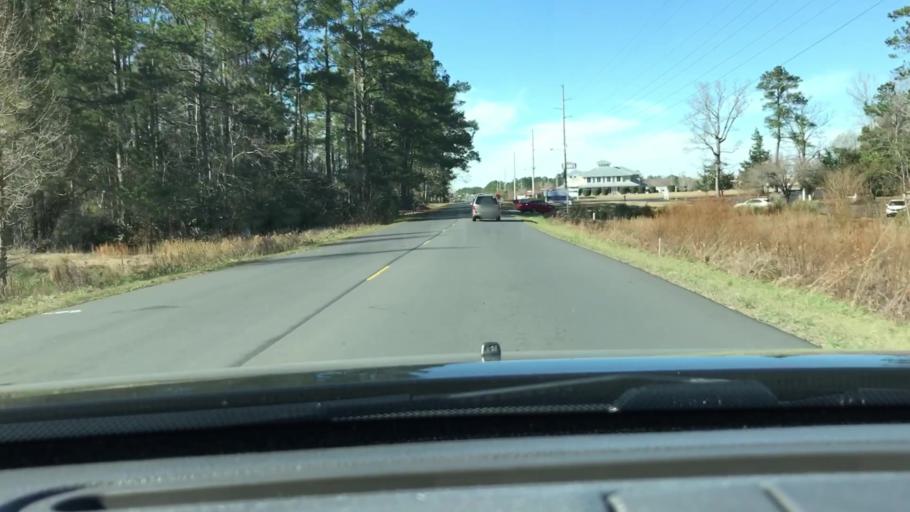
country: US
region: North Carolina
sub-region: Brunswick County
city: Shallotte
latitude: 33.9710
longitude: -78.3964
